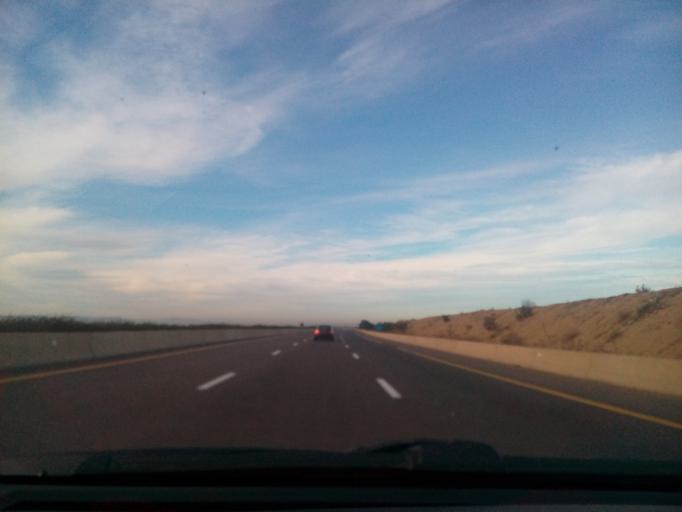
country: DZ
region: Mascara
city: Mascara
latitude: 35.6526
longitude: 0.1165
